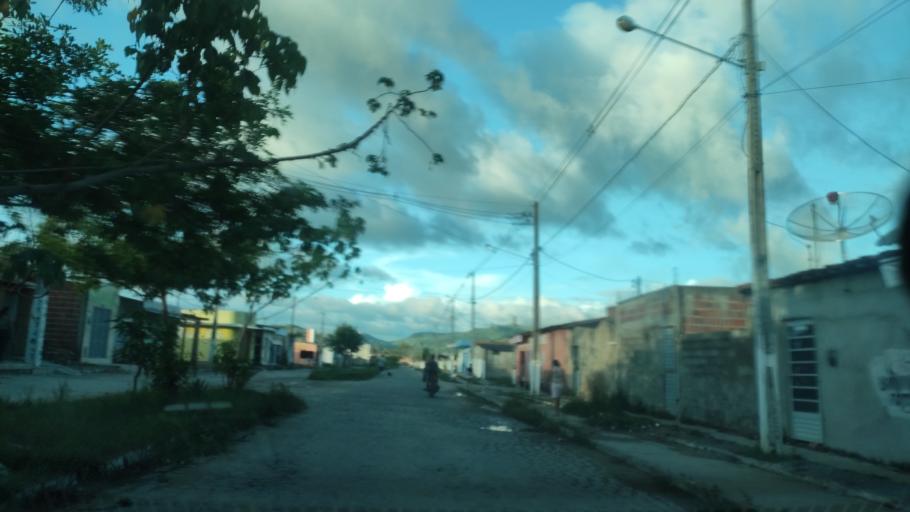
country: BR
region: Alagoas
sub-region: Uniao Dos Palmares
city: Uniao dos Palmares
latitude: -9.1485
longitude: -36.0053
